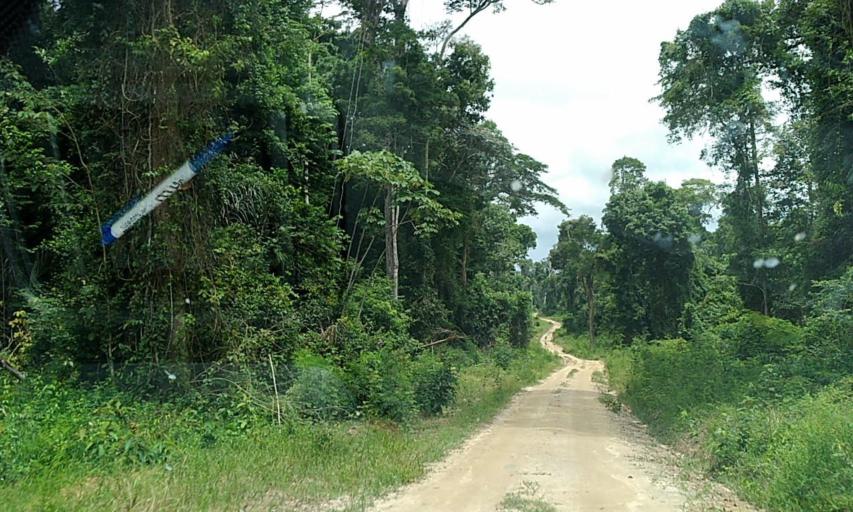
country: BR
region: Para
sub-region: Altamira
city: Altamira
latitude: -3.0542
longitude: -52.9100
